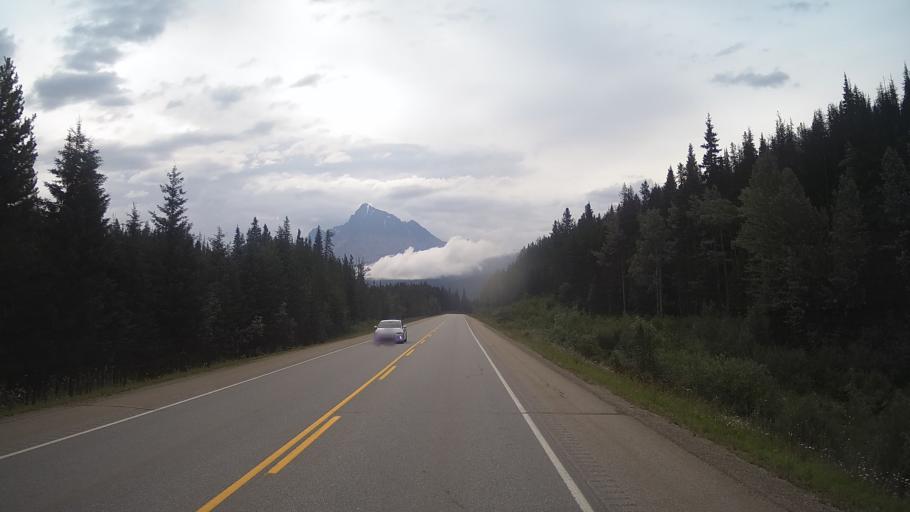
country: CA
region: Alberta
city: Jasper Park Lodge
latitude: 52.8588
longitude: -118.6348
